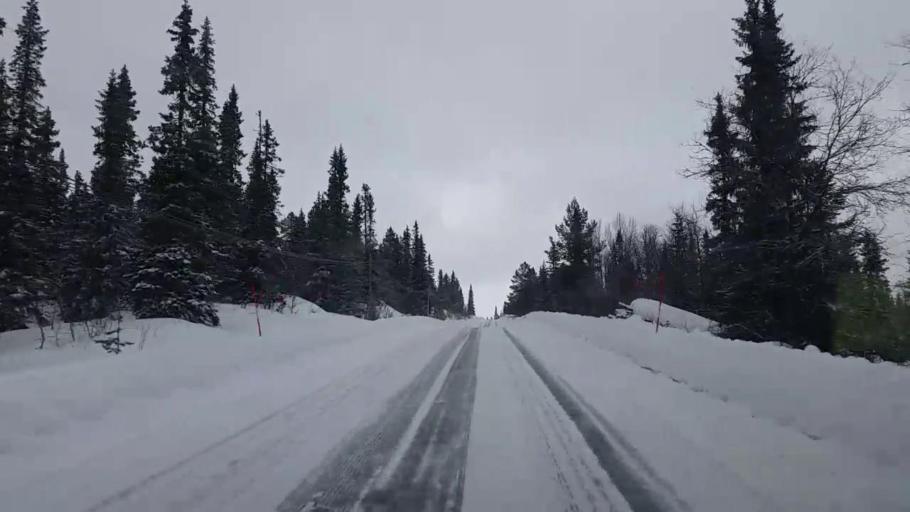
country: SE
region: Jaemtland
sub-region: Bergs Kommun
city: Hoverberg
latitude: 62.4883
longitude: 14.1187
